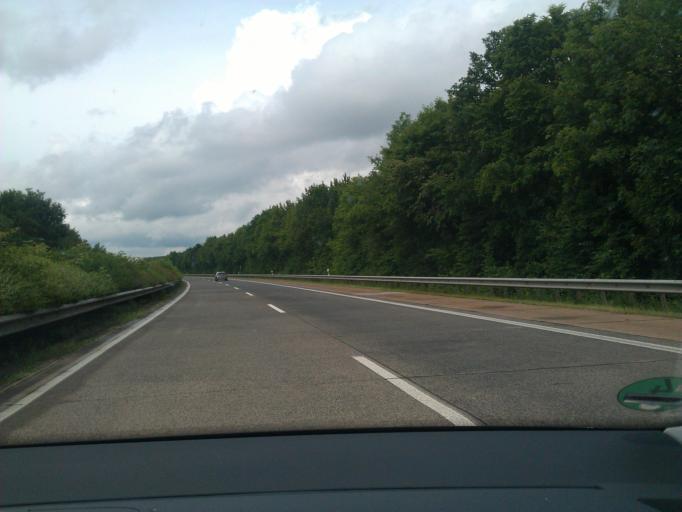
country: DE
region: Rheinland-Pfalz
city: Rivenich
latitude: 49.8877
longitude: 6.8508
